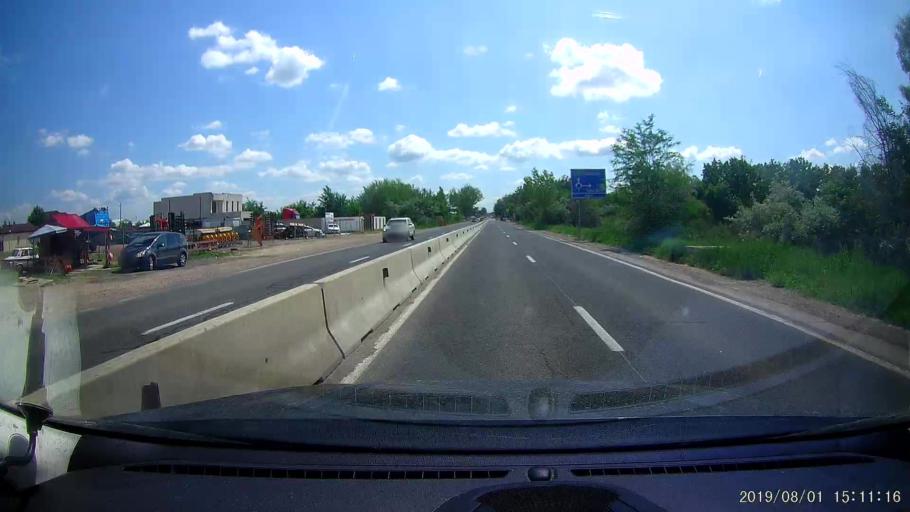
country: RO
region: Braila
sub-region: Comuna Chiscani
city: Chiscani
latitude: 45.2192
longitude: 27.9255
